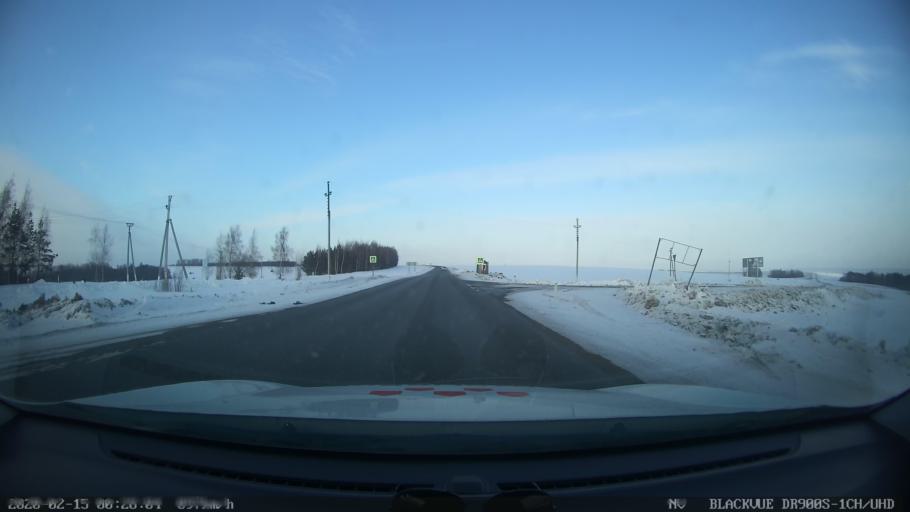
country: RU
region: Tatarstan
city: Verkhniy Uslon
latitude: 55.6372
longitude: 48.8734
